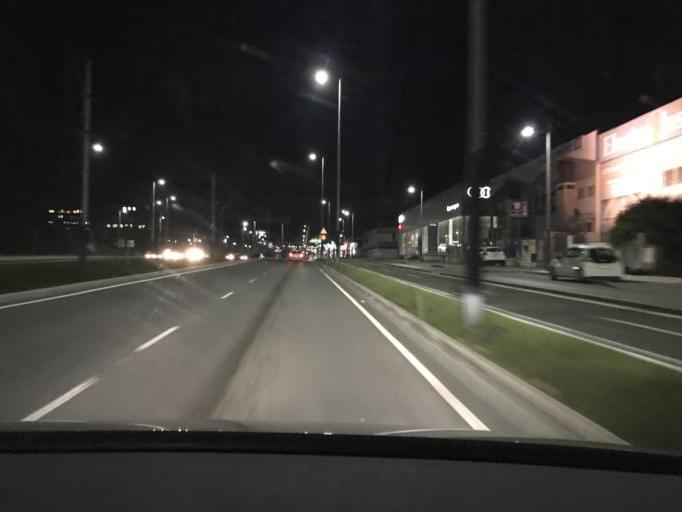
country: ES
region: Andalusia
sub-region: Provincia de Jaen
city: Jaen
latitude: 37.7992
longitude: -3.7787
